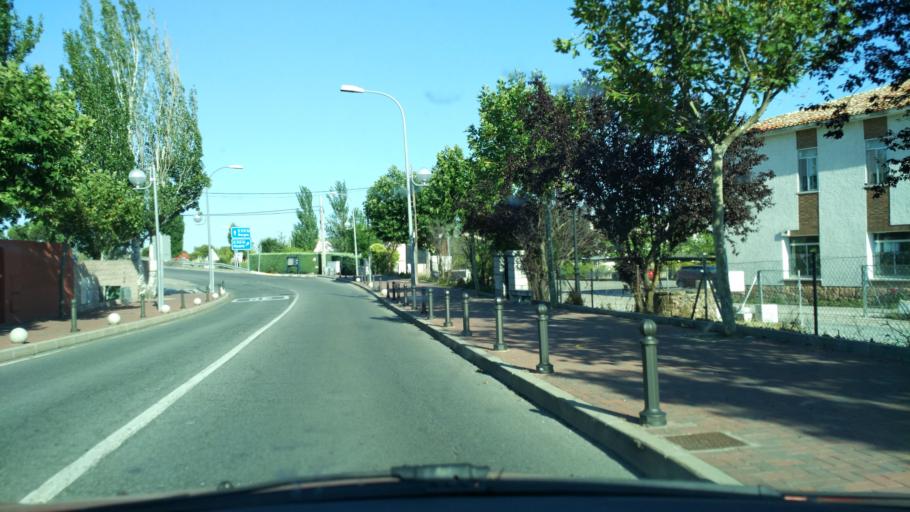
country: ES
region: Madrid
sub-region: Provincia de Madrid
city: Pedrezuela
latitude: 40.7441
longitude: -3.5942
